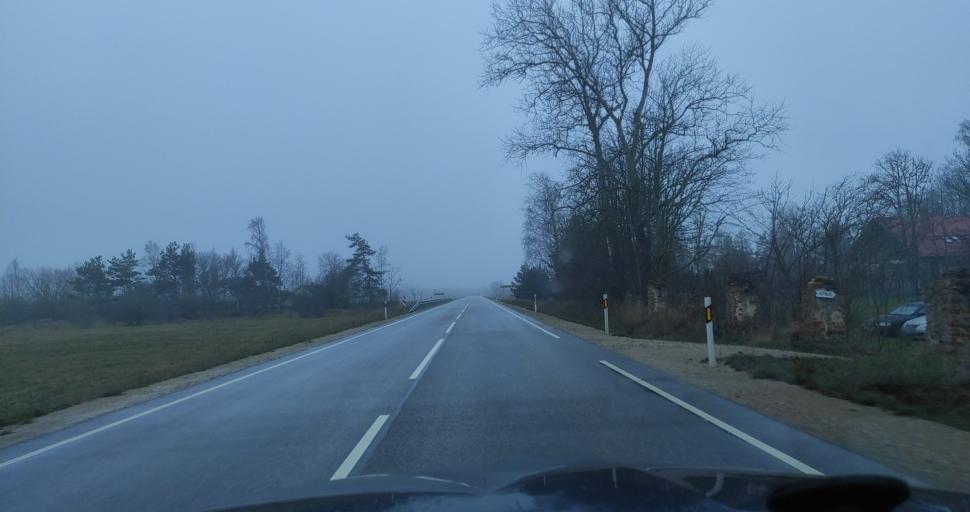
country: LV
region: Pavilostas
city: Pavilosta
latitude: 56.9358
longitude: 21.2759
